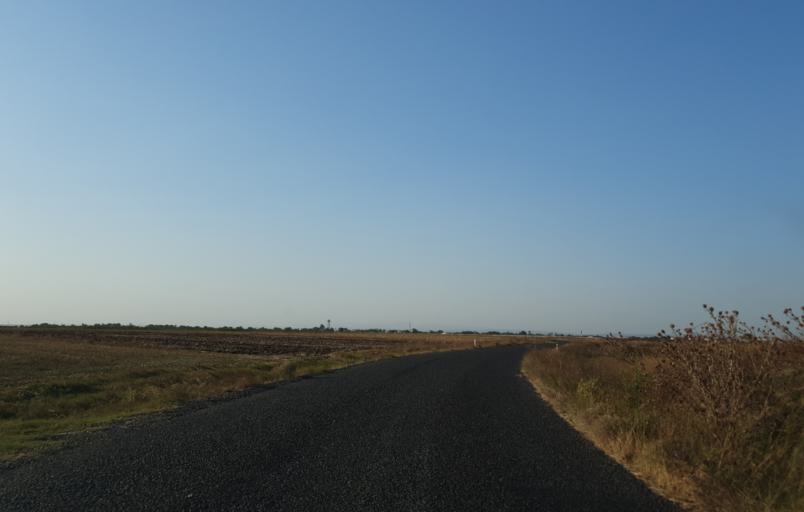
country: TR
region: Tekirdag
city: Beyazkoy
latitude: 41.4211
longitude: 27.7621
